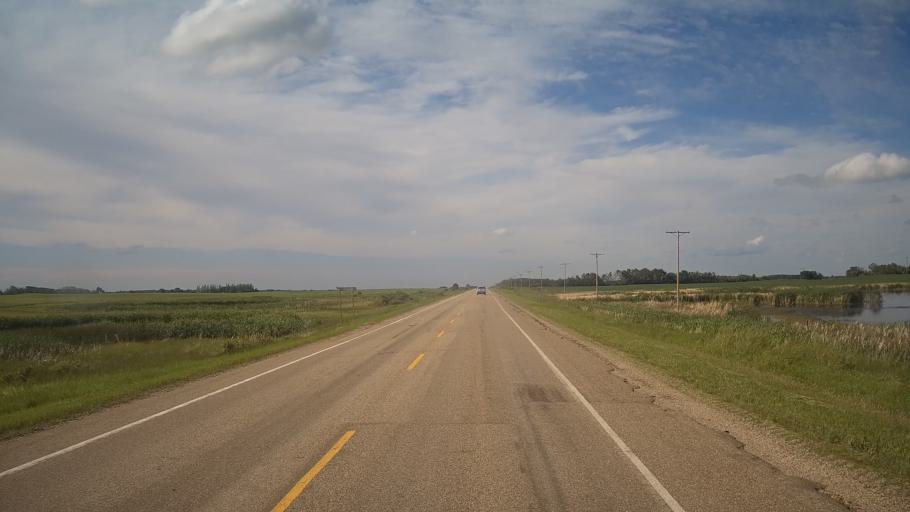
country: CA
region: Saskatchewan
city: Foam Lake
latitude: 51.6093
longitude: -103.8459
